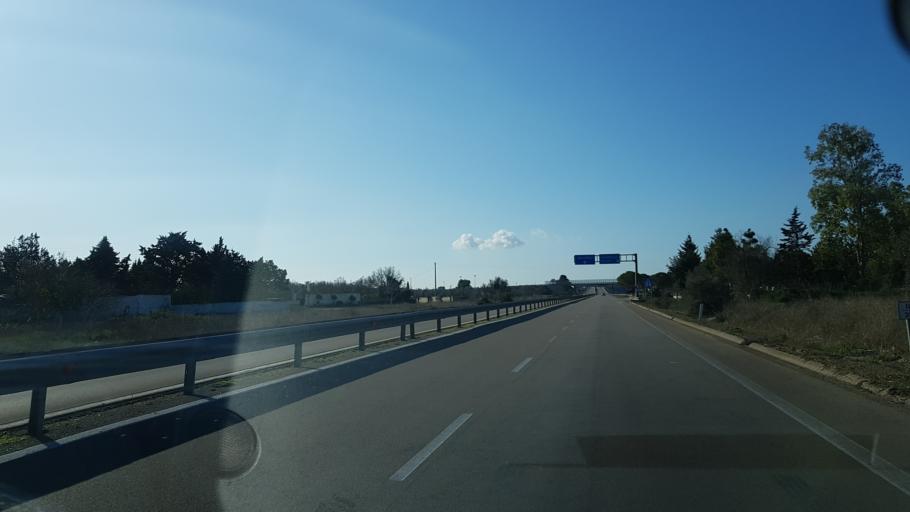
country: IT
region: Apulia
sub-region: Provincia di Lecce
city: Galatone
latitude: 40.1226
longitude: 18.0499
